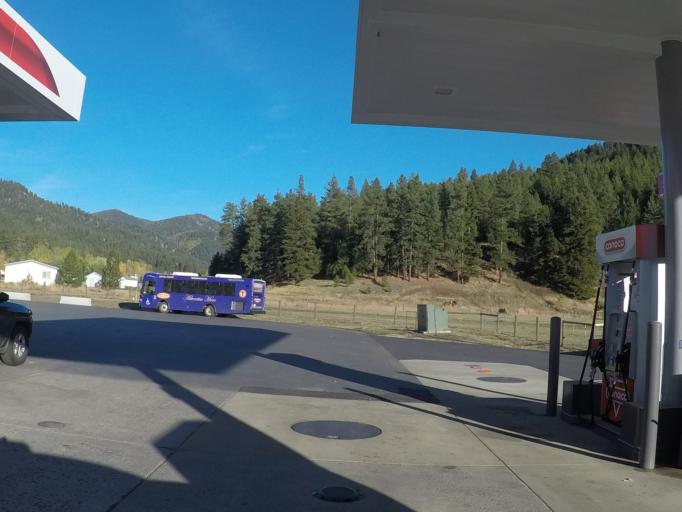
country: US
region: Montana
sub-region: Missoula County
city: Clinton
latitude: 46.7772
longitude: -113.7100
